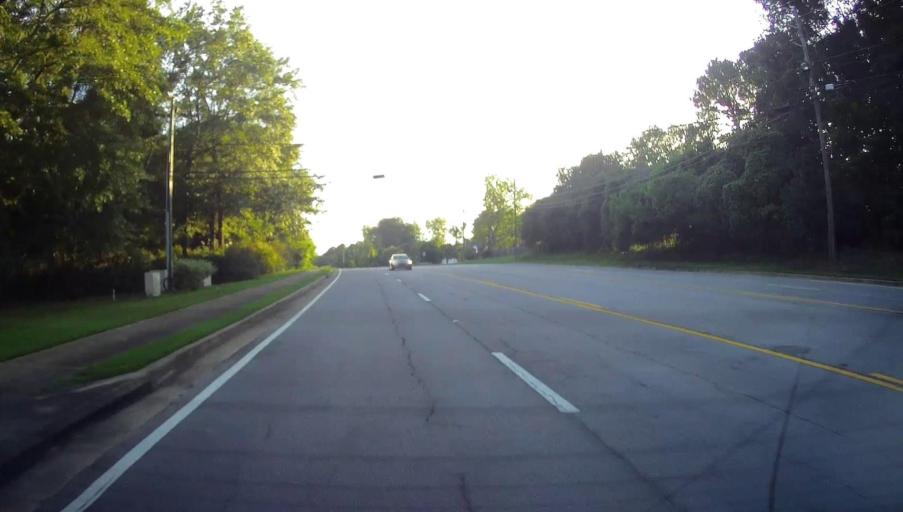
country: US
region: Georgia
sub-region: Muscogee County
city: Columbus
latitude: 32.5007
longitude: -84.9028
